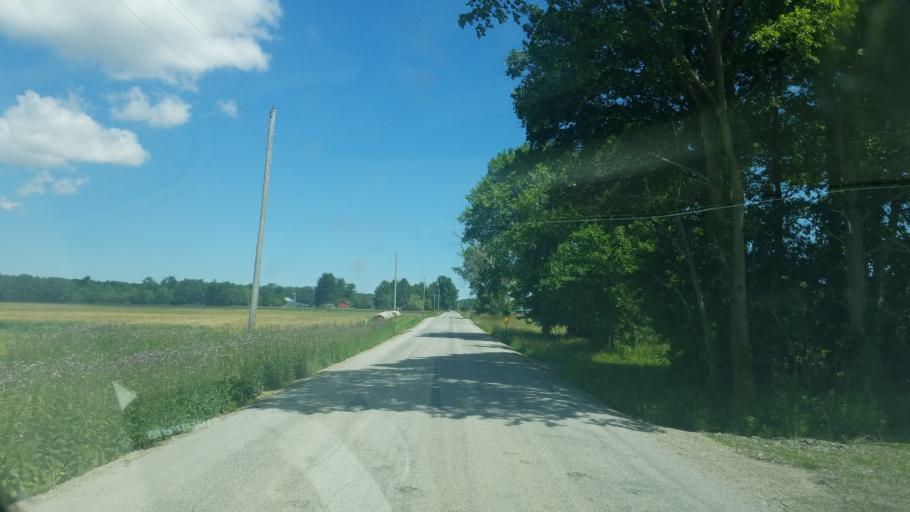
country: US
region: Ohio
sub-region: Huron County
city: New London
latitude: 41.1633
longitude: -82.3898
